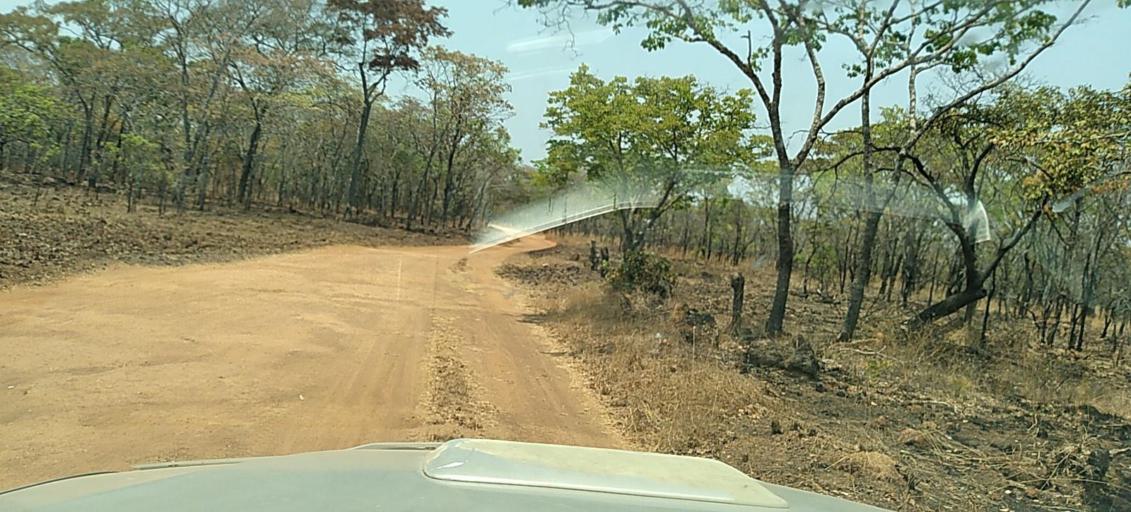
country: ZM
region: North-Western
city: Kasempa
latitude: -13.6082
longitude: 26.1862
